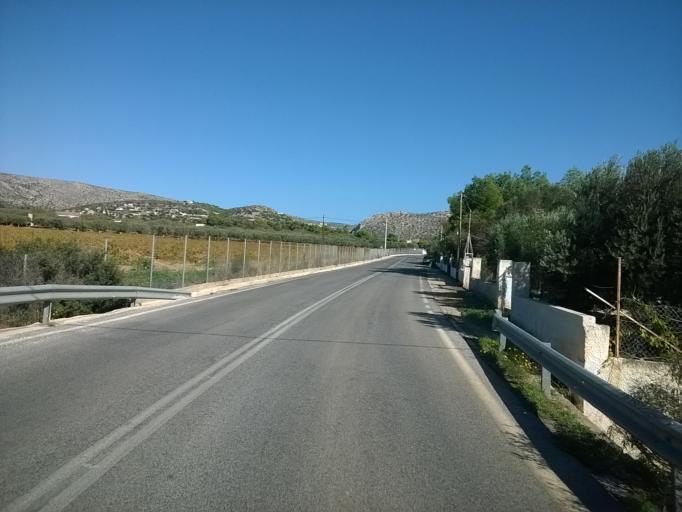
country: GR
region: Attica
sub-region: Nomarchia Anatolikis Attikis
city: Anavyssos
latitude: 37.7582
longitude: 23.9761
